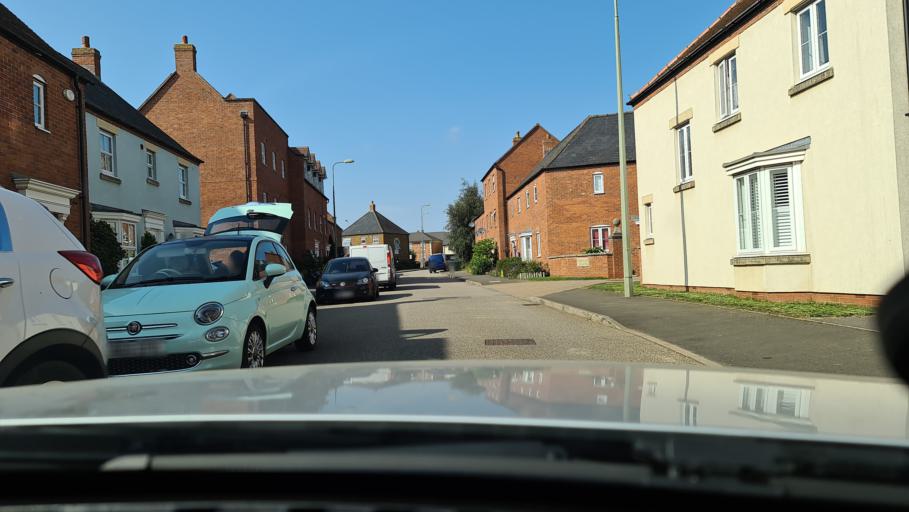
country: GB
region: England
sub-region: Oxfordshire
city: Hanwell
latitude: 52.0799
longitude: -1.3591
